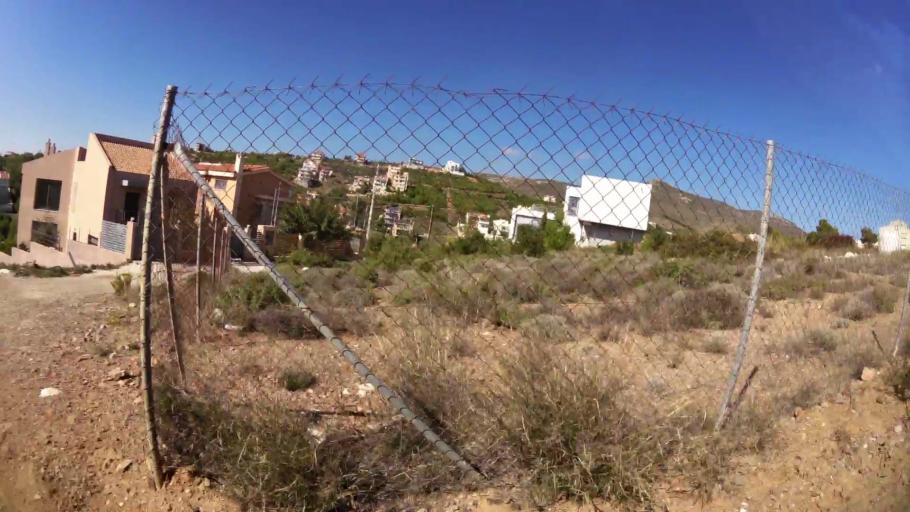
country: GR
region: Attica
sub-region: Nomarchia Anatolikis Attikis
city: Dioni
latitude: 38.0315
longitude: 23.9426
